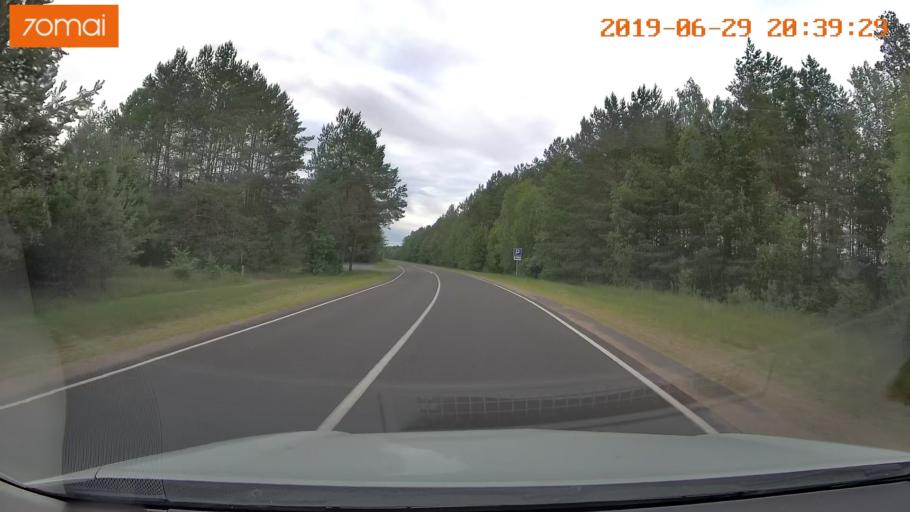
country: BY
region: Brest
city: Hantsavichy
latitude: 52.5633
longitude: 26.3624
